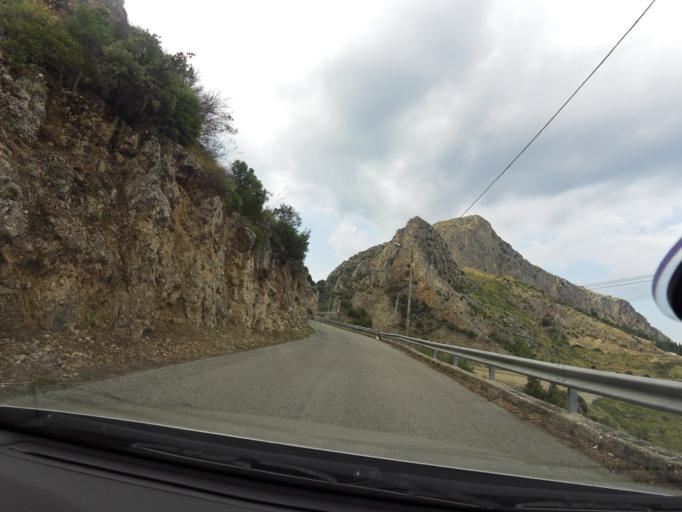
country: IT
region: Calabria
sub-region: Provincia di Reggio Calabria
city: Pazzano
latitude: 38.4704
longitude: 16.4556
